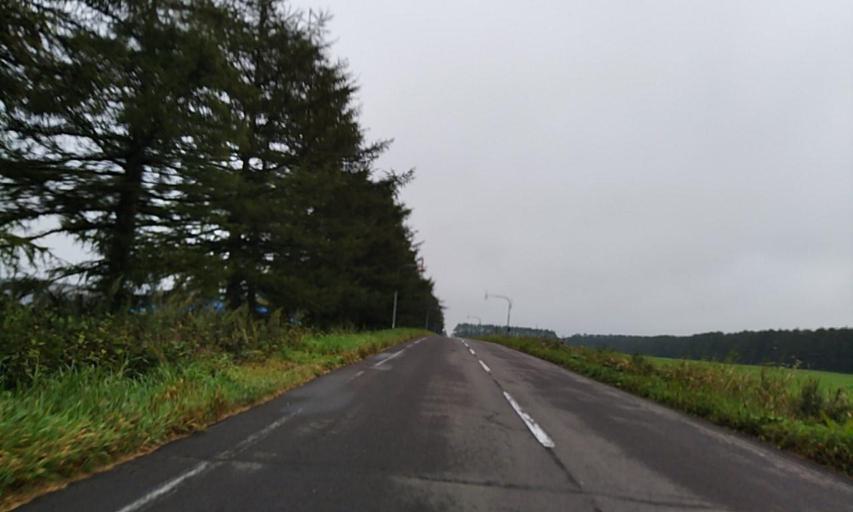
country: JP
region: Hokkaido
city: Shibetsu
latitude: 43.5176
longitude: 144.6808
